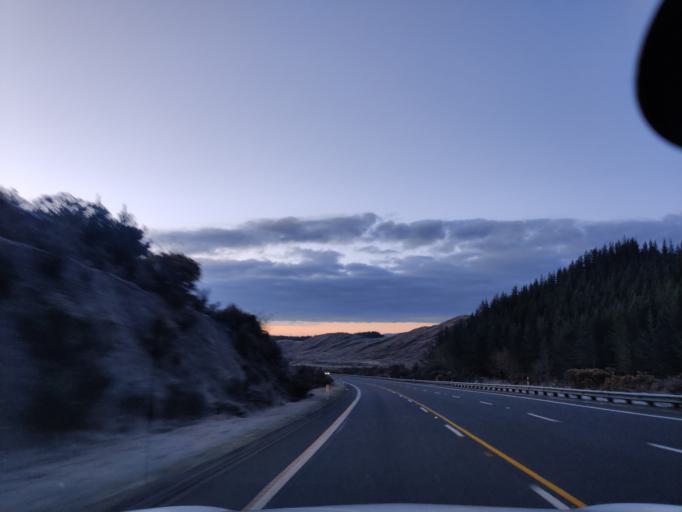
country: NZ
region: Waikato
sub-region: South Waikato District
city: Tokoroa
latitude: -38.3246
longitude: 175.9886
